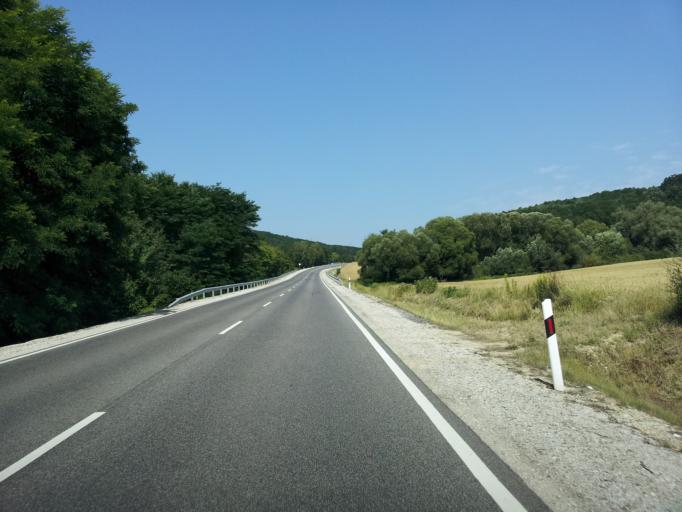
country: HU
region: Zala
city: Pacsa
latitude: 46.8099
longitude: 17.0654
